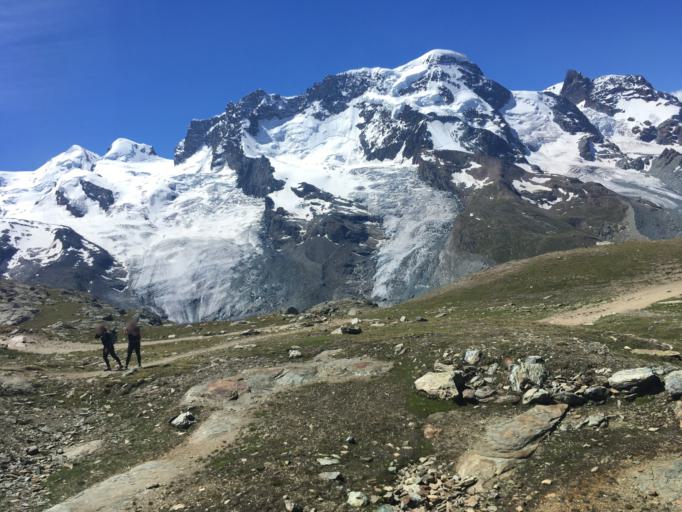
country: CH
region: Valais
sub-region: Visp District
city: Zermatt
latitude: 45.9851
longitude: 7.7704
